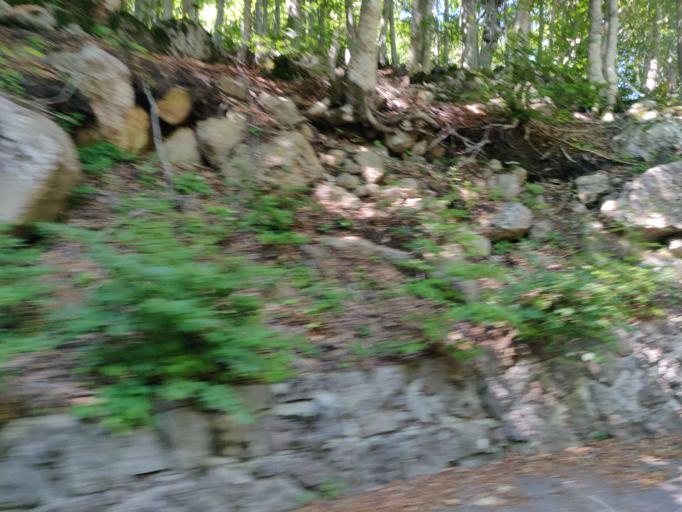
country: IT
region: Tuscany
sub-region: Provincia di Siena
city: Abbadia San Salvatore
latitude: 42.8898
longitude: 11.6280
